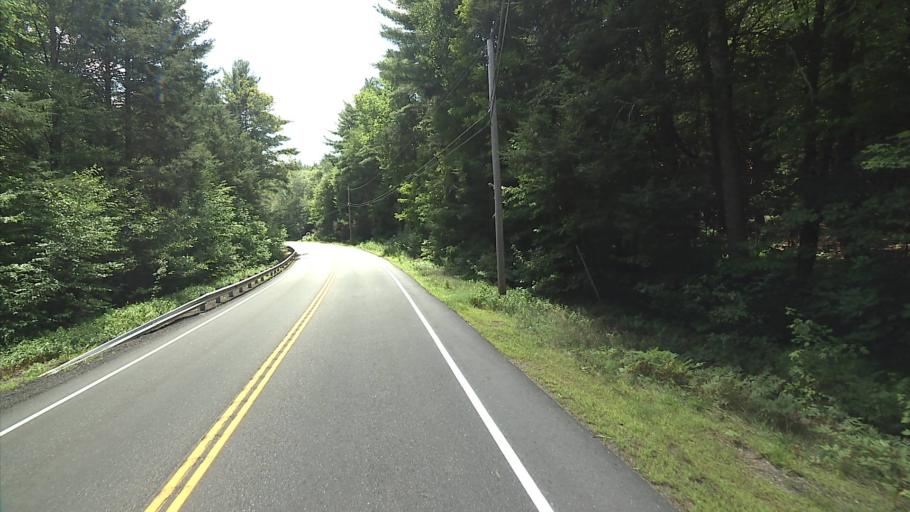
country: US
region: Massachusetts
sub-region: Worcester County
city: Southbridge
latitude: 41.9936
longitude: -72.0833
